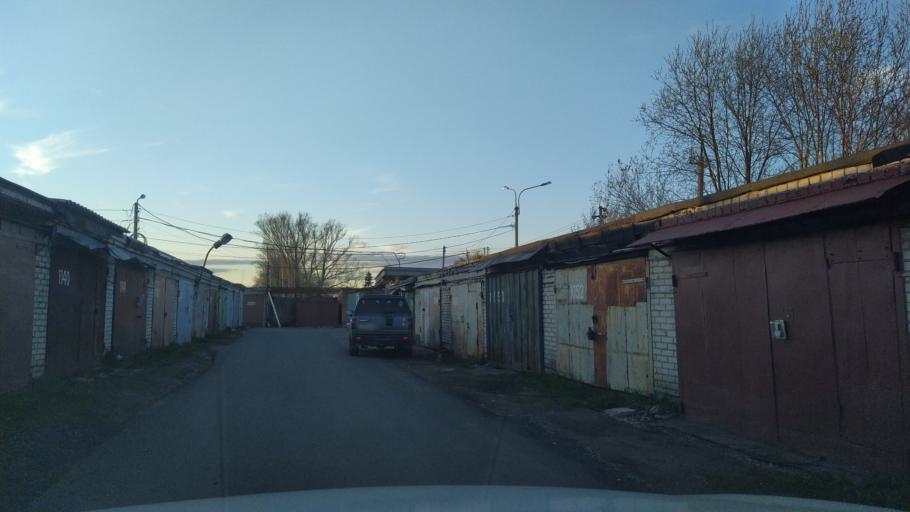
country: RU
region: St.-Petersburg
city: Pushkin
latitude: 59.6926
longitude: 30.3959
